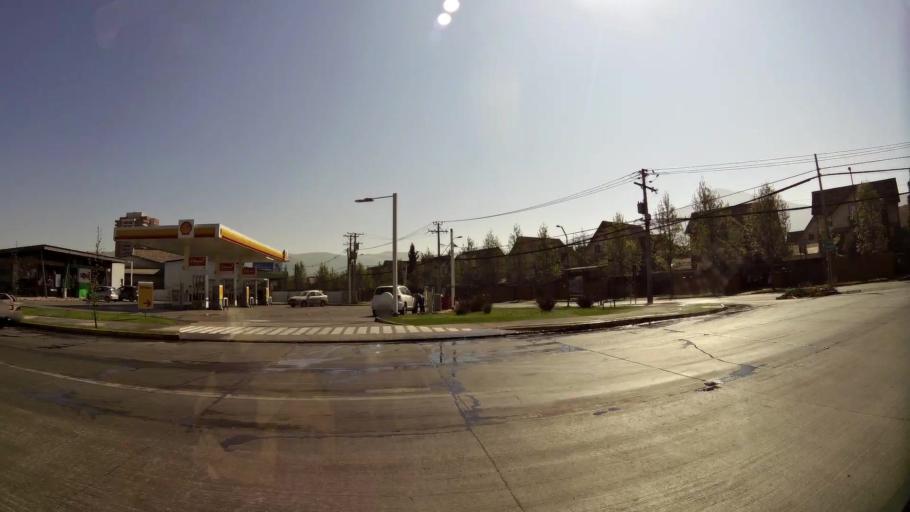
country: CL
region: Santiago Metropolitan
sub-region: Provincia de Chacabuco
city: Chicureo Abajo
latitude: -33.3641
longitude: -70.6748
